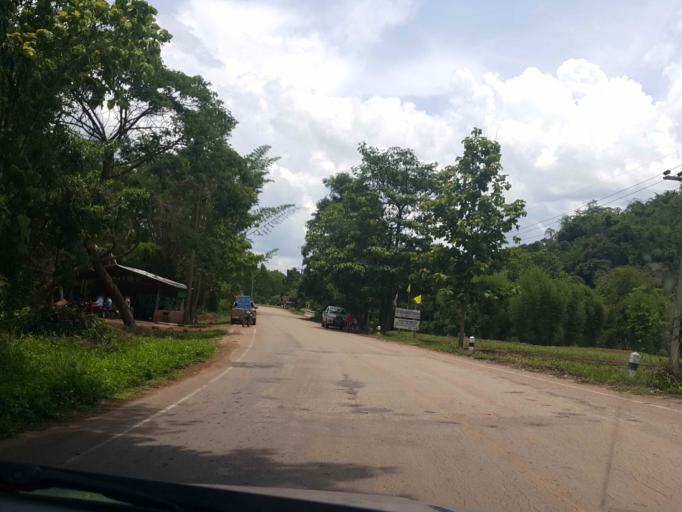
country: TH
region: Phayao
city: Chiang Muan
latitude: 18.8969
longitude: 100.1357
